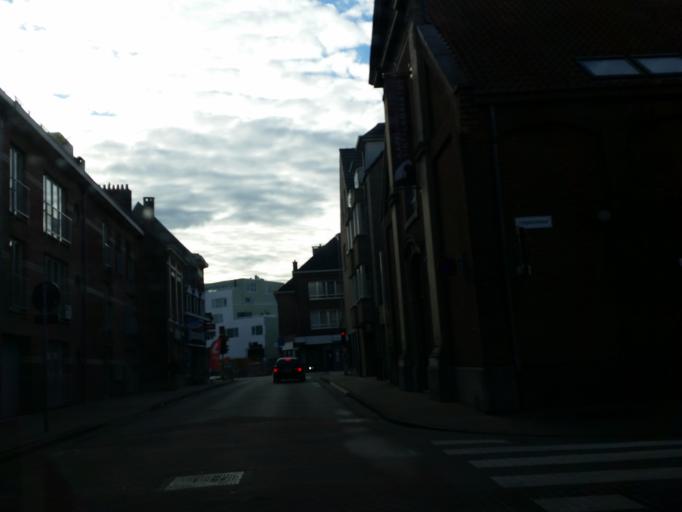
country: BE
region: Flanders
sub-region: Provincie Antwerpen
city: Kapellen
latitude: 51.2780
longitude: 4.4174
